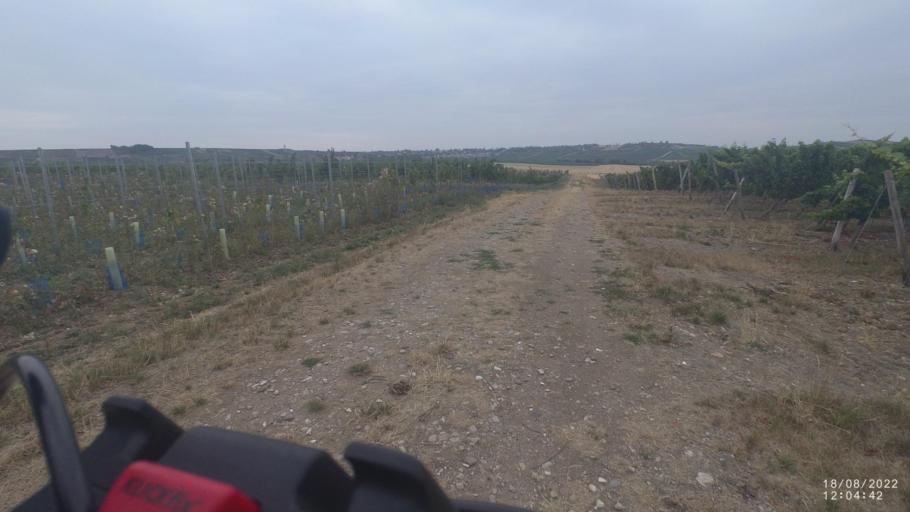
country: DE
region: Rheinland-Pfalz
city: Gau-Weinheim
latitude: 49.8526
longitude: 8.0598
